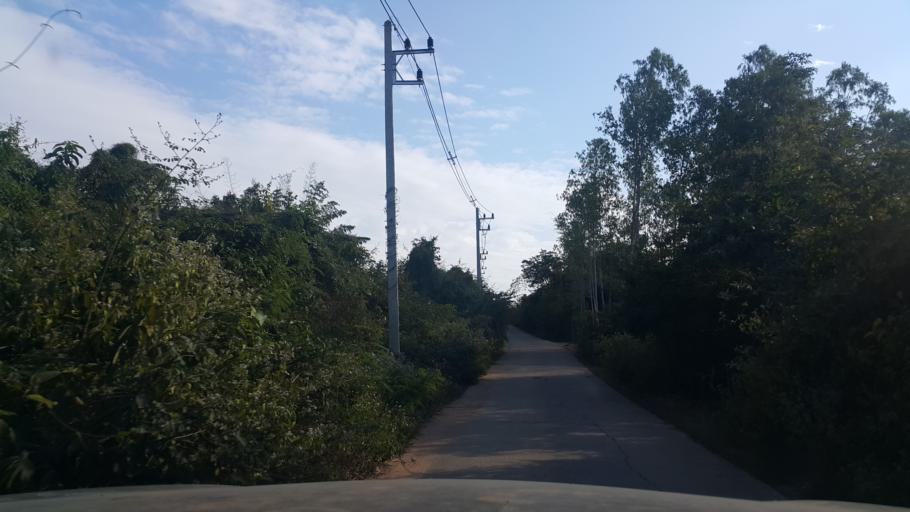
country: TH
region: Lampang
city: Hang Chat
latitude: 18.3030
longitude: 99.3519
